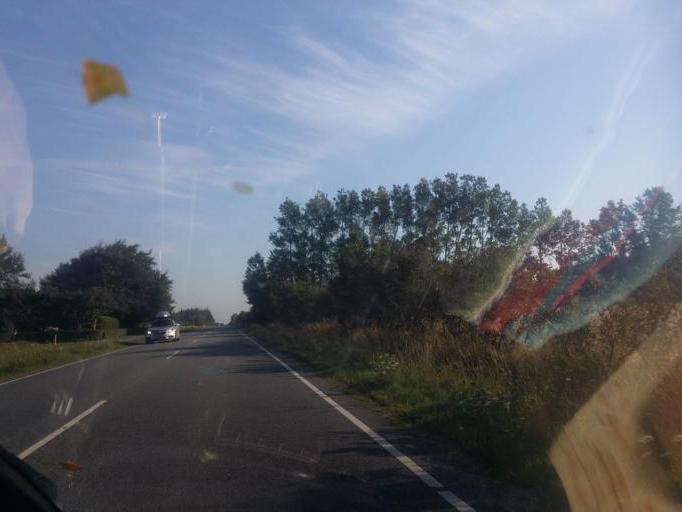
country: DK
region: South Denmark
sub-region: Esbjerg Kommune
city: Ribe
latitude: 55.2932
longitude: 8.7388
